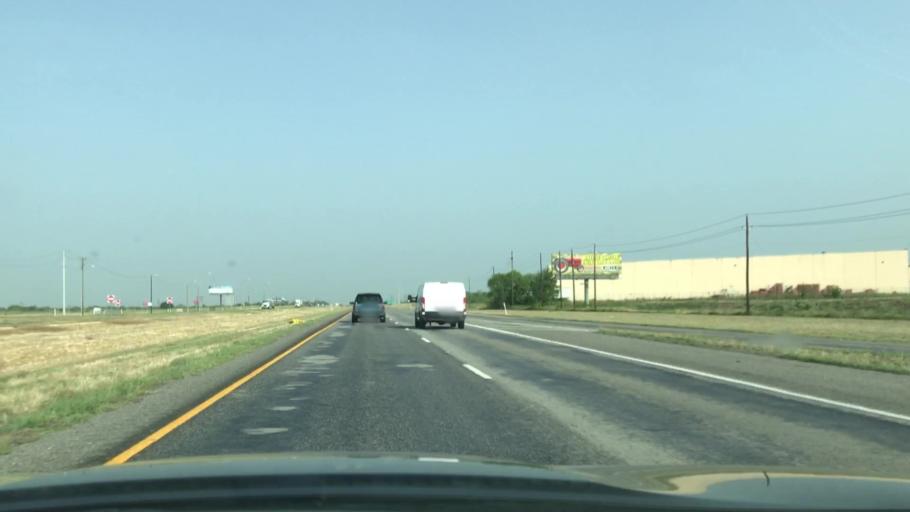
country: US
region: Texas
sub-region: Kaufman County
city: Terrell
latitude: 32.7222
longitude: -96.3225
